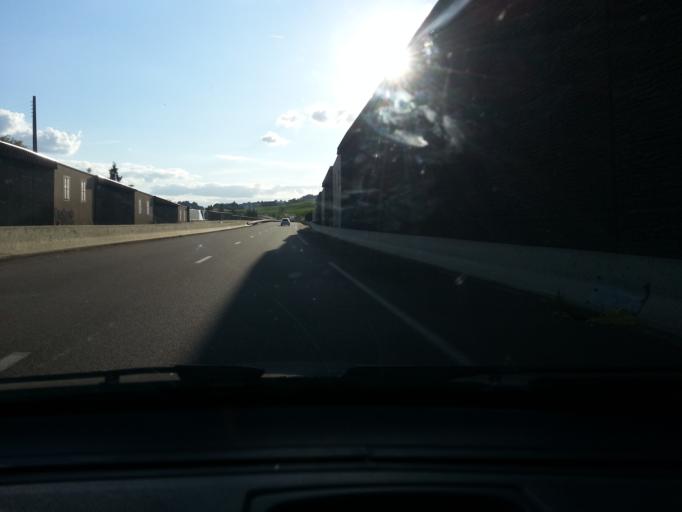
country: FR
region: Bourgogne
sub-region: Departement de Saone-et-Loire
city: Givry
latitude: 46.7568
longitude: 4.7098
